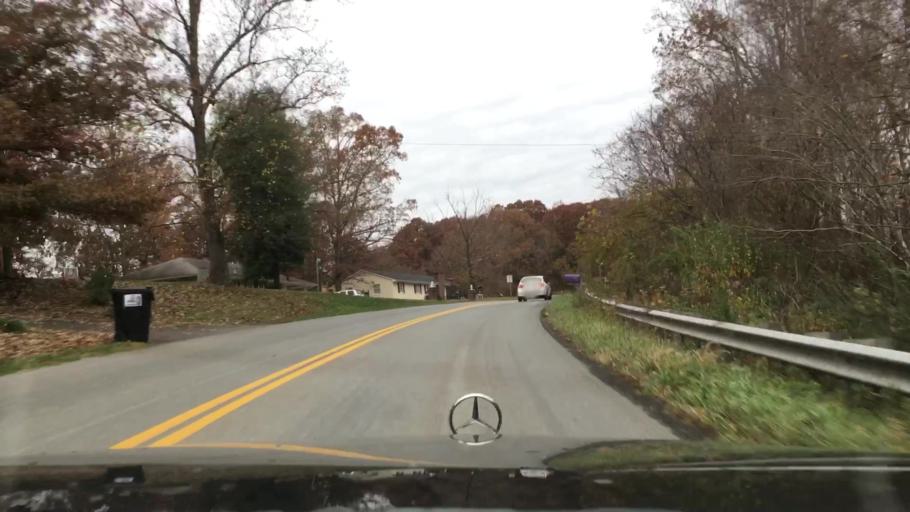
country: US
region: Virginia
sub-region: Campbell County
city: Timberlake
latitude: 37.2905
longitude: -79.2766
